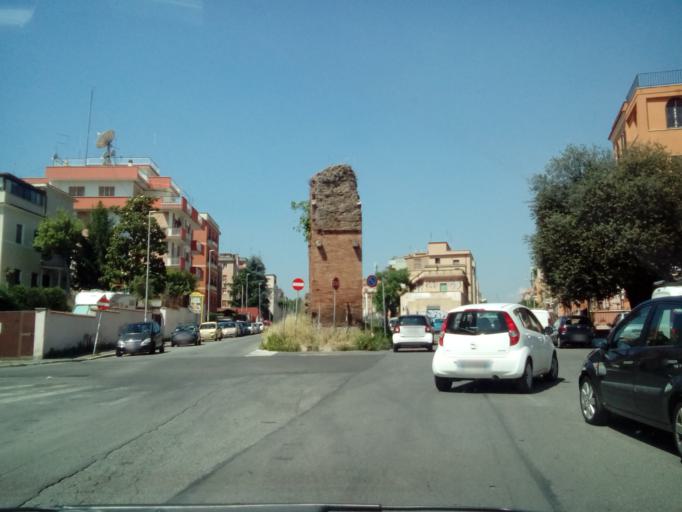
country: IT
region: Latium
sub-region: Citta metropolitana di Roma Capitale
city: Rome
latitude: 41.8780
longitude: 12.5714
